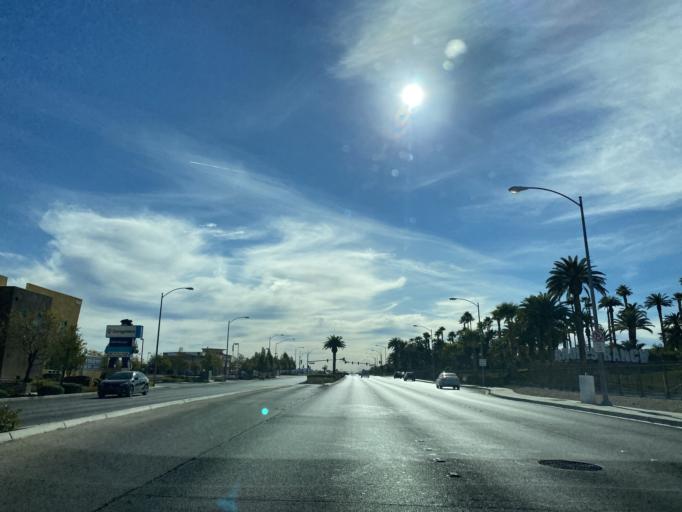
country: US
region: Nevada
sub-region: Clark County
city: Enterprise
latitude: 36.0501
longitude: -115.2792
